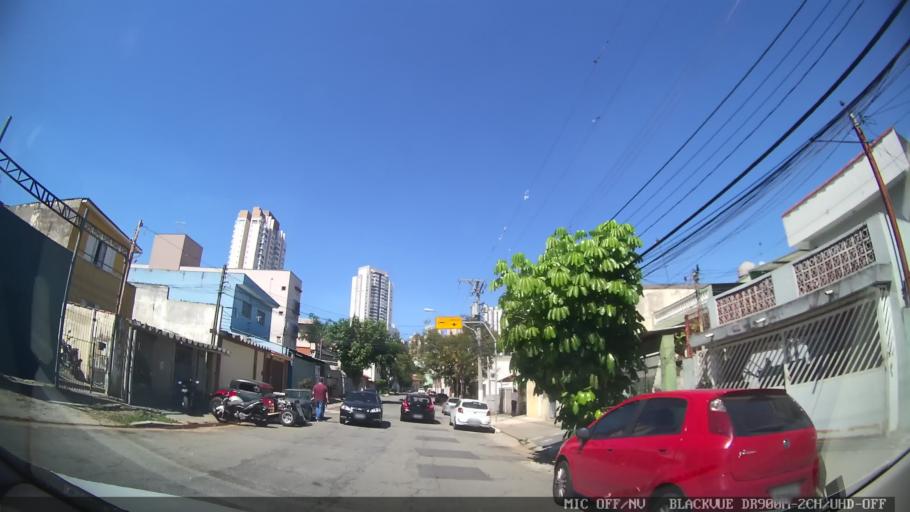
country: BR
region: Sao Paulo
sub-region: Sao Paulo
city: Sao Paulo
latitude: -23.4959
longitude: -46.6477
